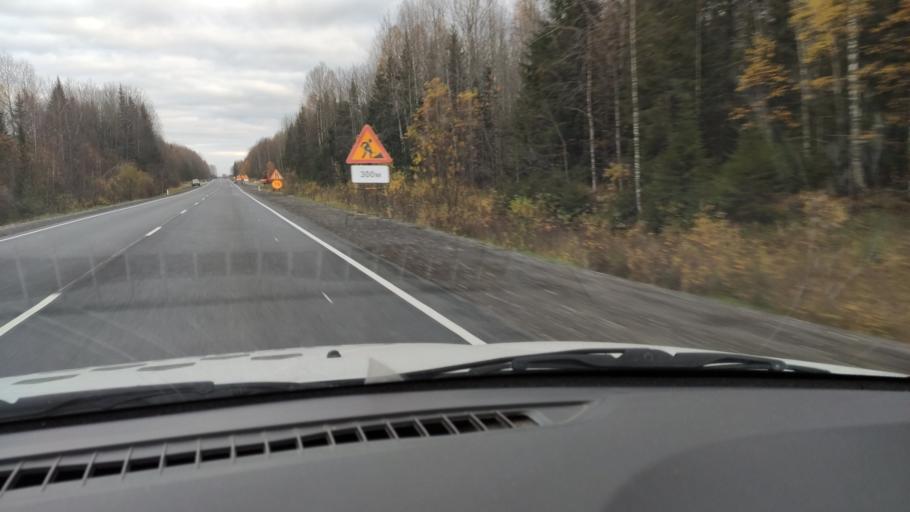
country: RU
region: Kirov
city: Chernaya Kholunitsa
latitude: 58.8797
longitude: 51.4468
